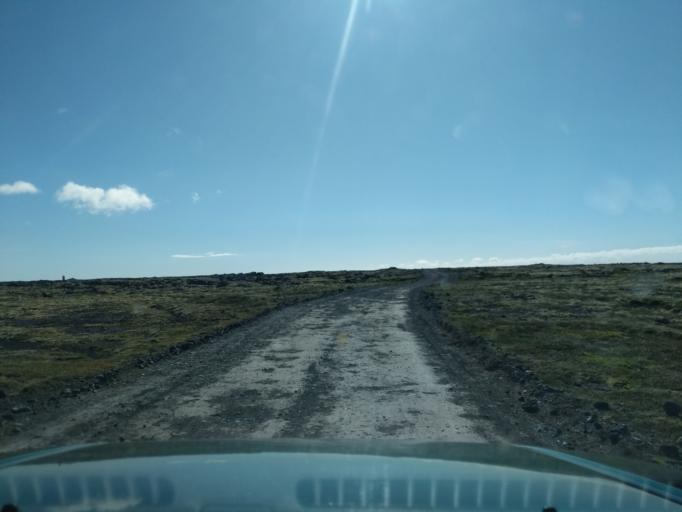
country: IS
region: West
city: Olafsvik
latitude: 64.8723
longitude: -24.0245
